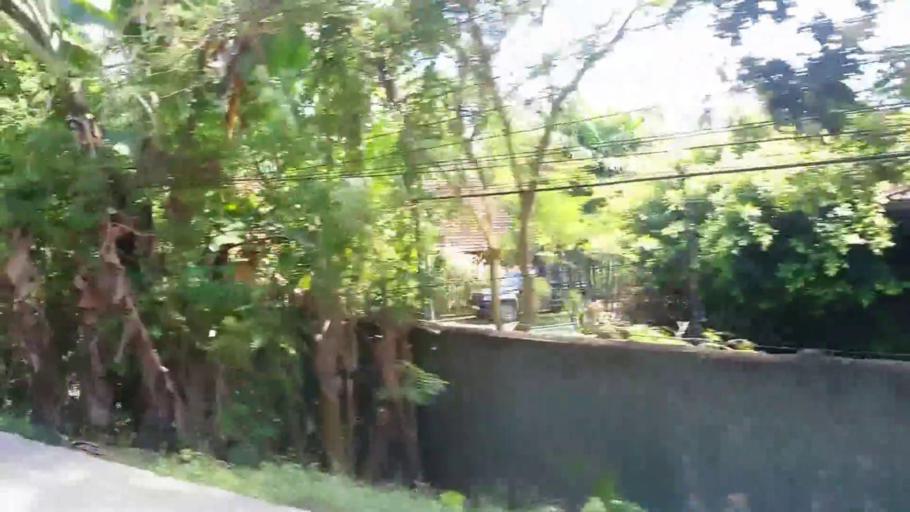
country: LK
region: Southern
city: Hikkaduwa
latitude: 6.1704
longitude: 80.0876
